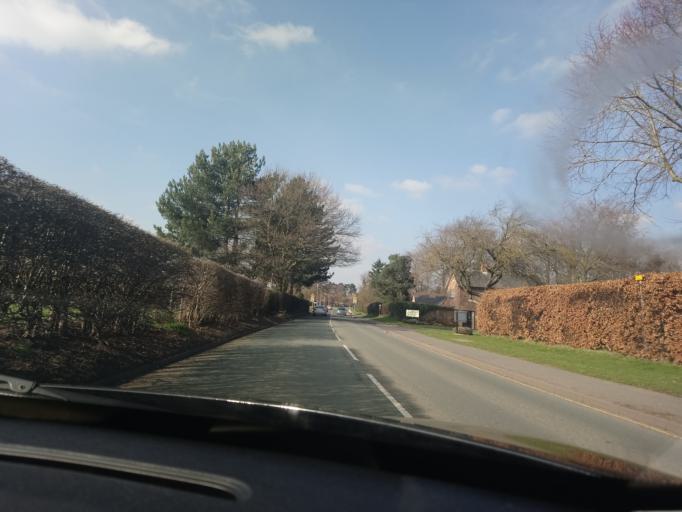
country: GB
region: England
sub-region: Shropshire
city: Shrewsbury
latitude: 52.6952
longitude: -2.7211
